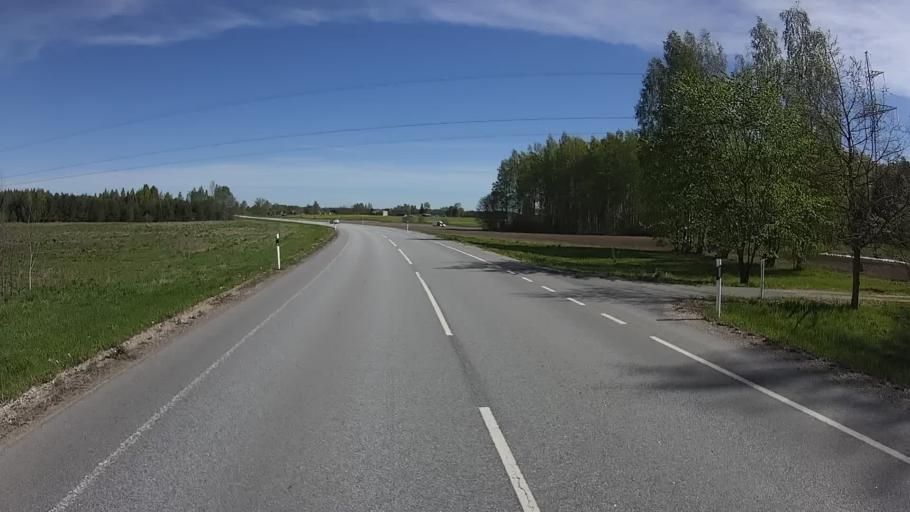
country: RU
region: Pskov
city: Pechory
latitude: 57.9295
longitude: 27.5738
